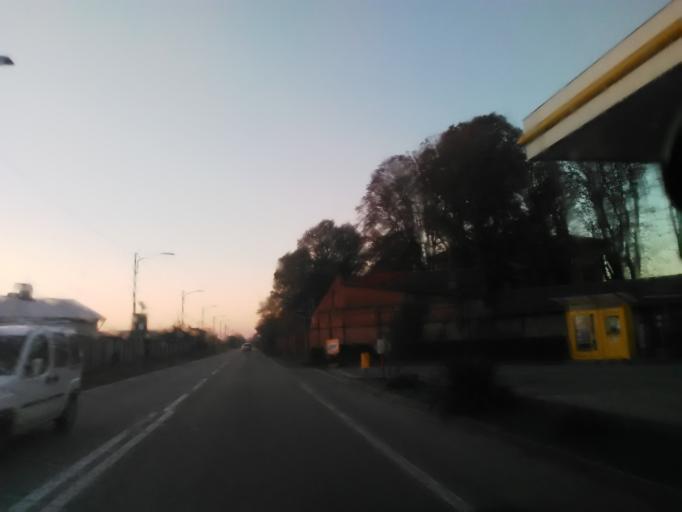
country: IT
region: Piedmont
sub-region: Provincia di Vercelli
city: Santhia
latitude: 45.3624
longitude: 8.1716
